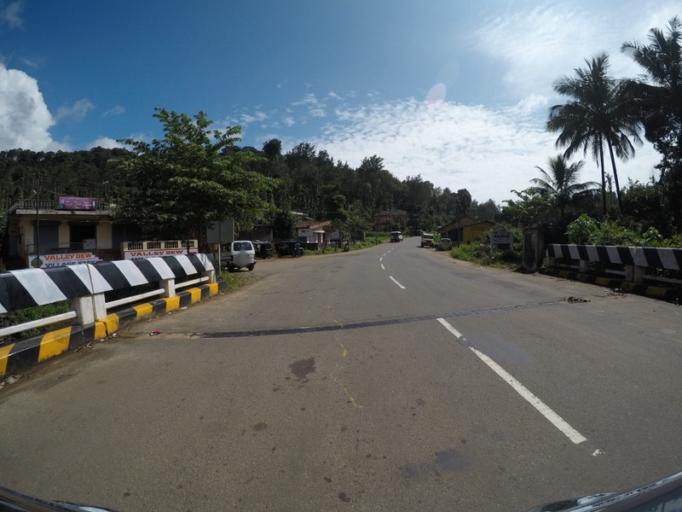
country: IN
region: Karnataka
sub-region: Kodagu
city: Suntikoppa
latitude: 12.4870
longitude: 75.7948
